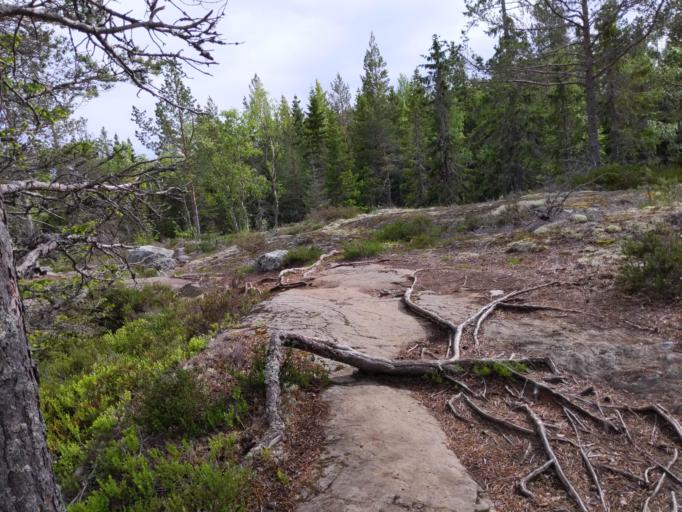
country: SE
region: Vaesternorrland
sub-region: OErnskoeldsviks Kommun
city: Ornskoldsvik
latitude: 63.1916
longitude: 18.6995
